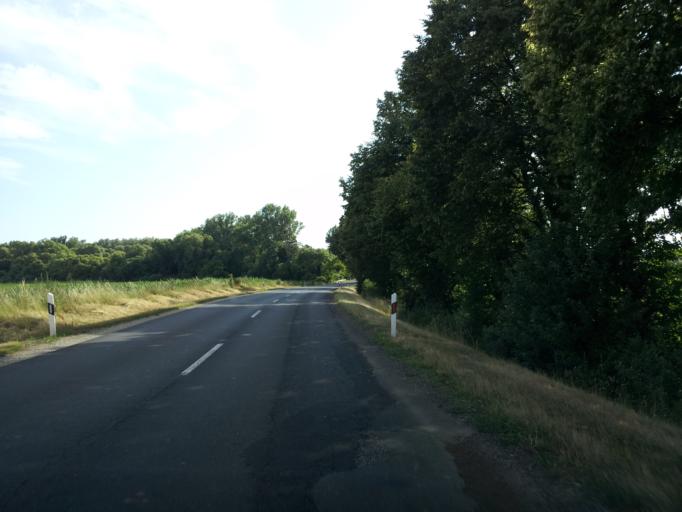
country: HU
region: Veszprem
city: Urkut
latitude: 46.9910
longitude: 17.7220
